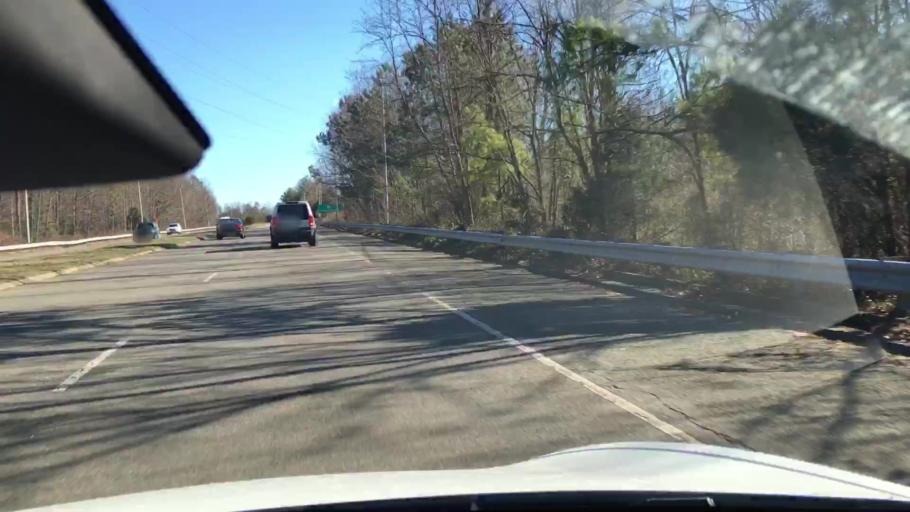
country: US
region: Virginia
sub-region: Chesterfield County
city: Bon Air
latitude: 37.5467
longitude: -77.5608
